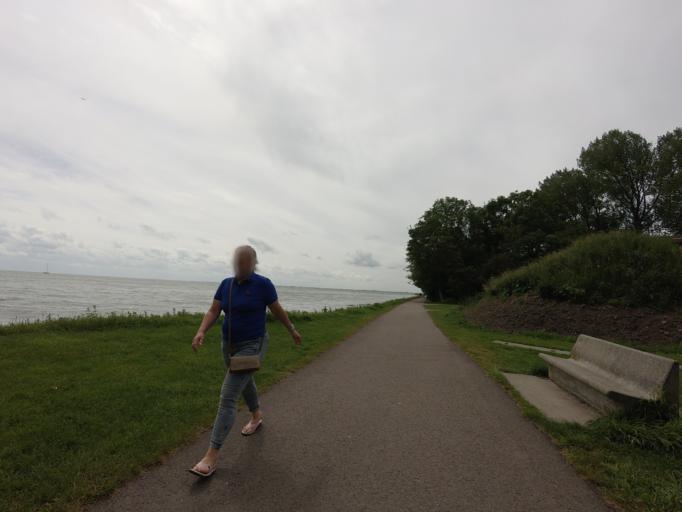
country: NL
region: North Holland
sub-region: Gemeente Hoorn
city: Hoorn
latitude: 52.6373
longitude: 5.0715
